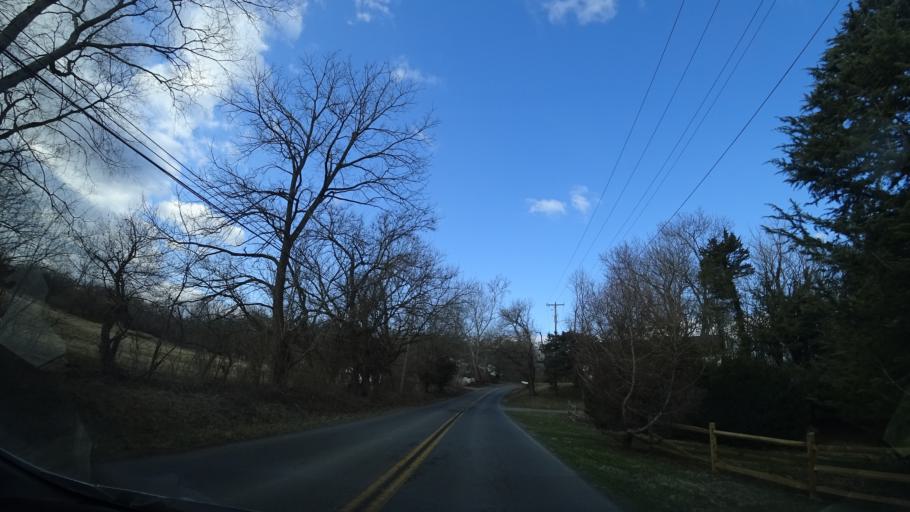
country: US
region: Virginia
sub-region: Warren County
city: Shenandoah Farms
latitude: 39.0646
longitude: -78.0321
